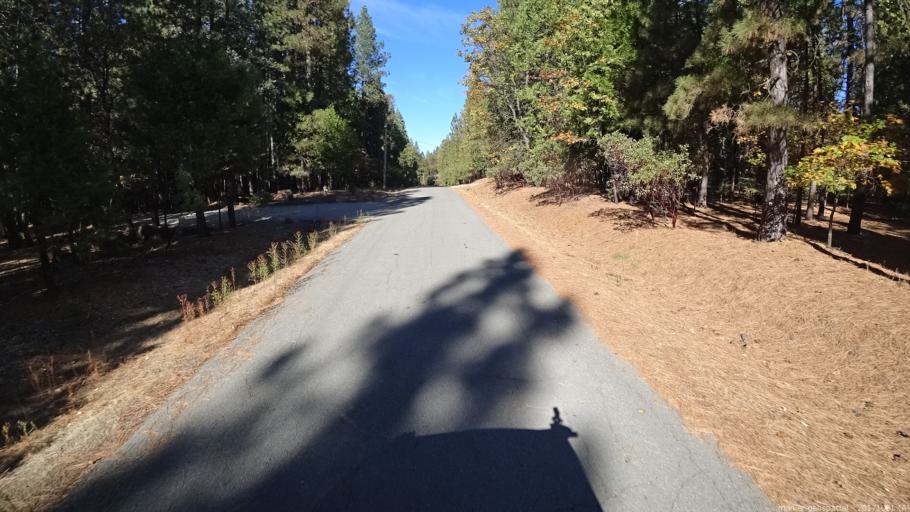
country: US
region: California
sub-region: Shasta County
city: Shingletown
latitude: 40.4851
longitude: -121.8857
